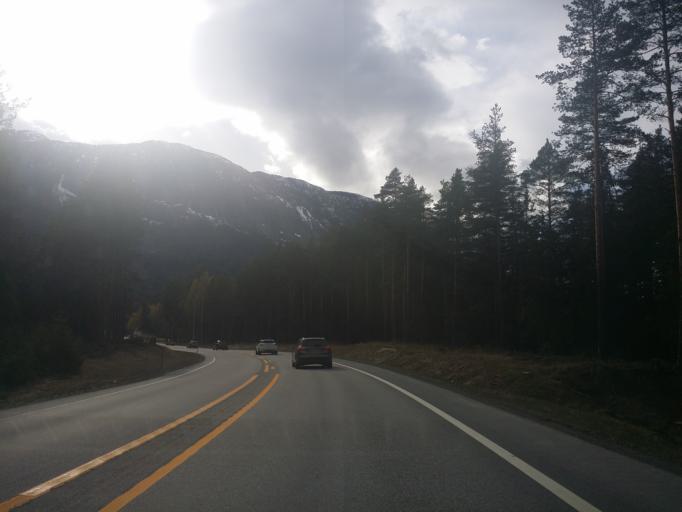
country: NO
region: Buskerud
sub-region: Fla
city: Fla
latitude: 60.4454
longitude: 9.3068
